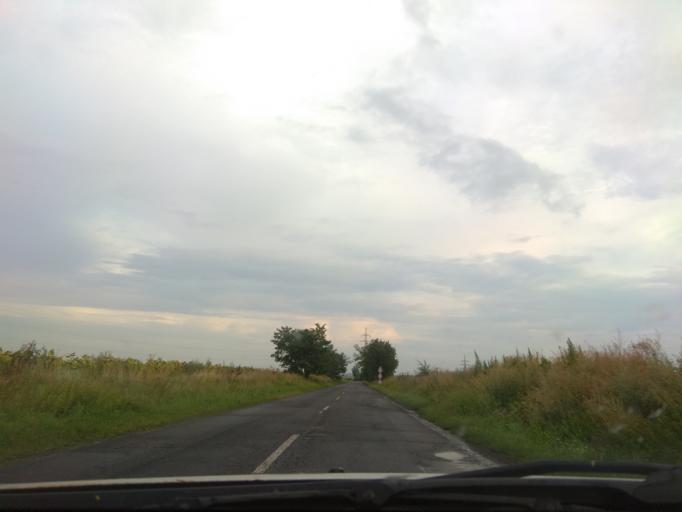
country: HU
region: Borsod-Abauj-Zemplen
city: Gesztely
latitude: 48.1283
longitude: 20.9728
